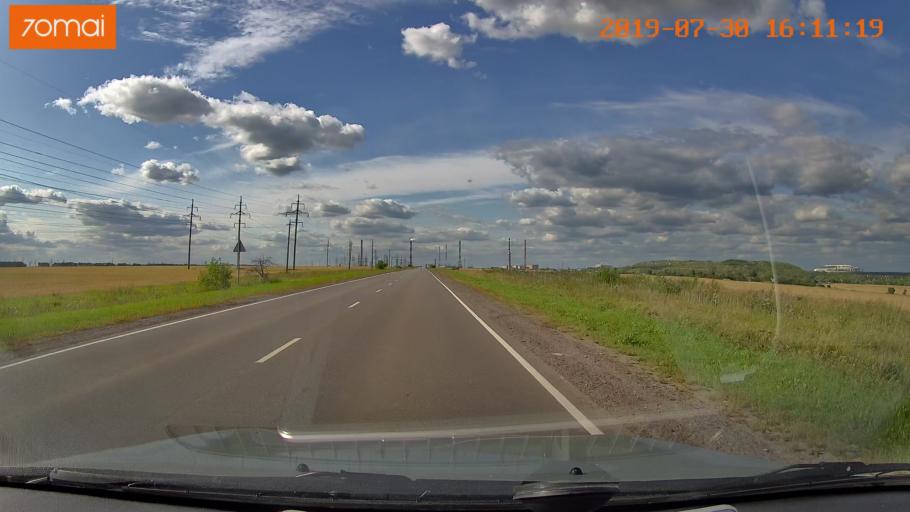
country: RU
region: Moskovskaya
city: Lopatinskiy
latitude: 55.2741
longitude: 38.7121
